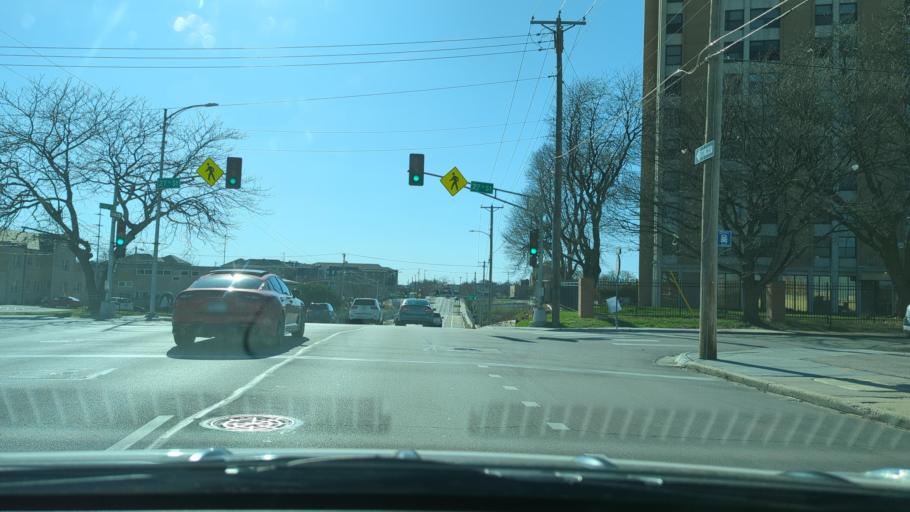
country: US
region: Nebraska
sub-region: Douglas County
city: Omaha
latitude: 41.2536
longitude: -95.9515
